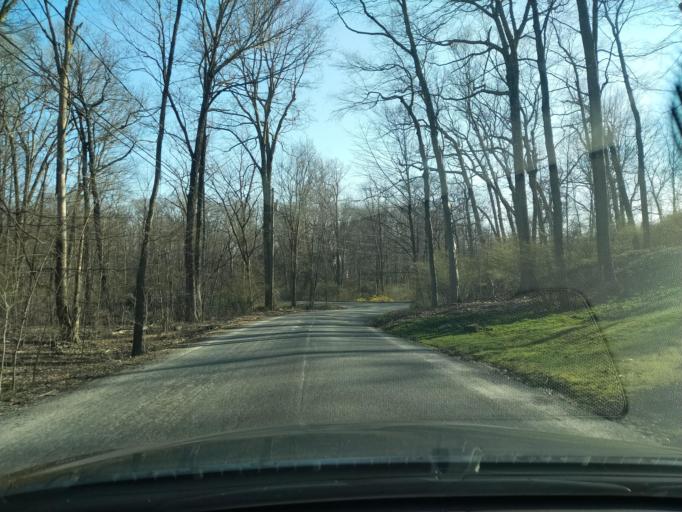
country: US
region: Connecticut
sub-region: Fairfield County
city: Newtown
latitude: 41.3824
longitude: -73.2920
